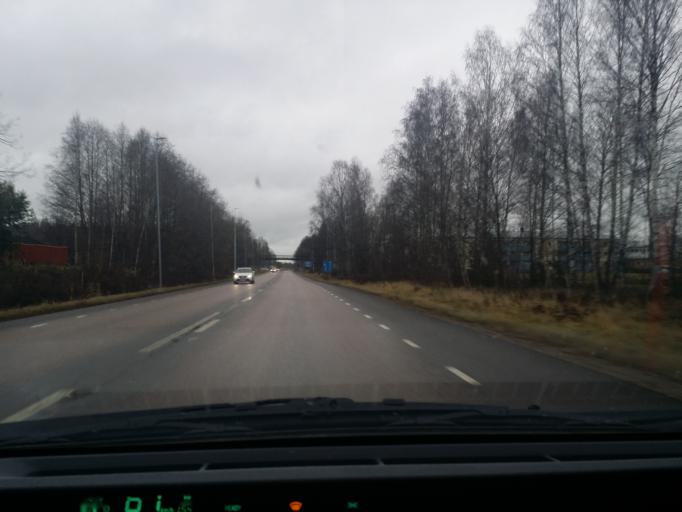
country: SE
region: Vaestmanland
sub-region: Sala Kommun
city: Sala
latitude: 59.9118
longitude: 16.5870
